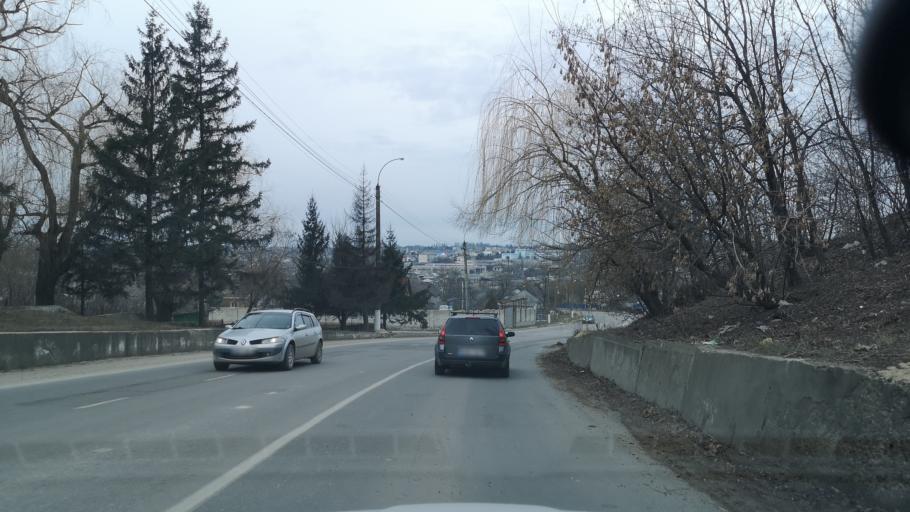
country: MD
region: Raionul Edinet
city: Edinet
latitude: 48.1631
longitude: 27.3221
